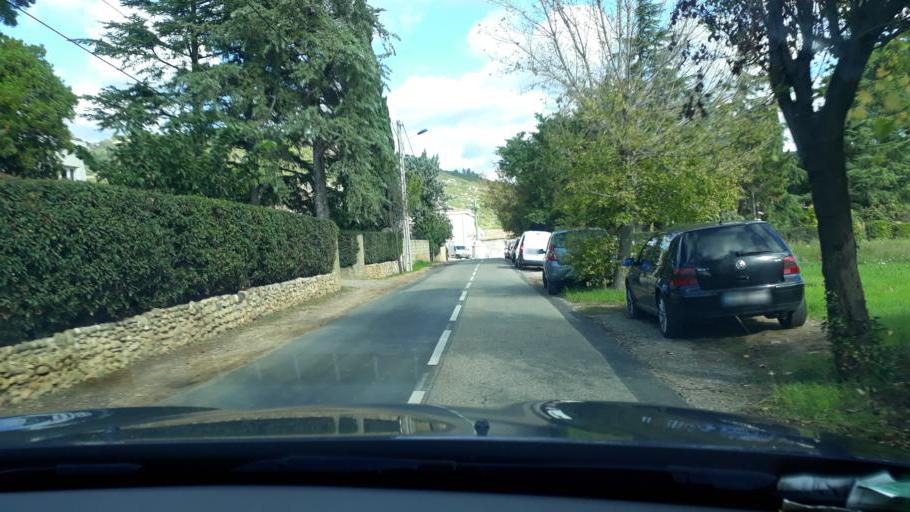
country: FR
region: Languedoc-Roussillon
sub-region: Departement de l'Herault
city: Saint-Jean-de-Fos
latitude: 43.7004
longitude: 3.5486
